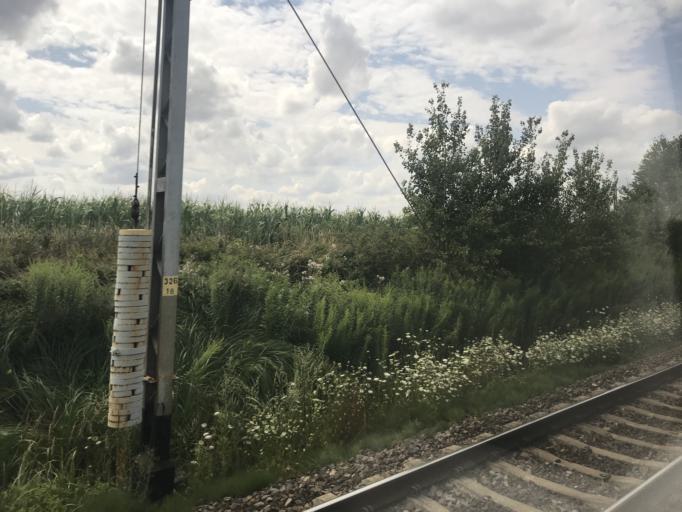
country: PL
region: Greater Poland Voivodeship
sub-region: Powiat poznanski
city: Dopiewo
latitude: 52.3465
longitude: 16.6371
